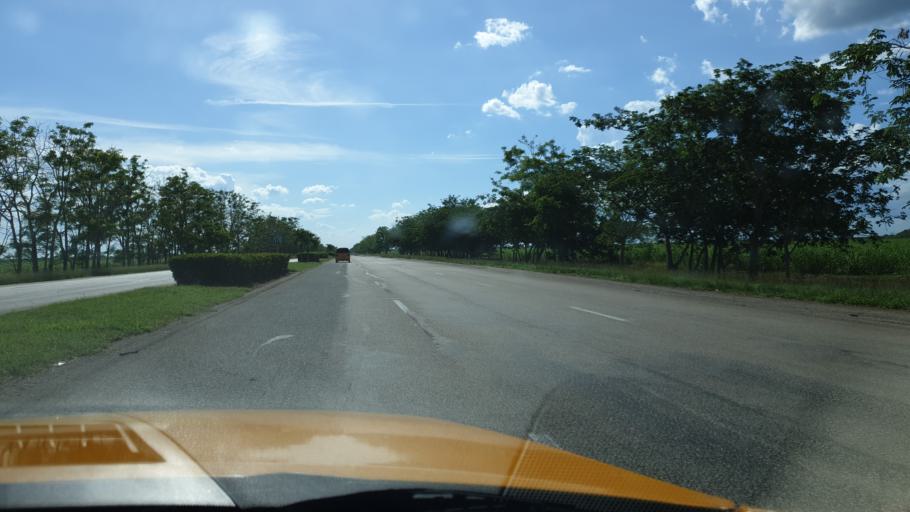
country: CU
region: Cienfuegos
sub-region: Municipio de Aguada de Pasajeros
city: Aguada de Pasajeros
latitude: 22.4120
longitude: -80.8969
